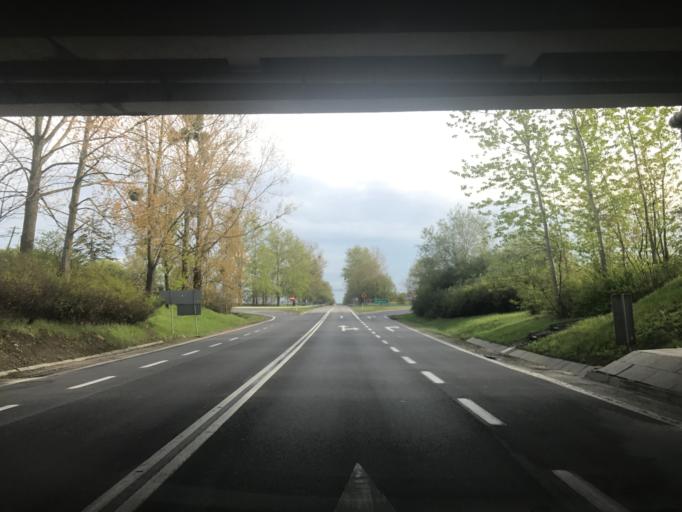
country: PL
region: Pomeranian Voivodeship
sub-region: Powiat tczewski
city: Subkowy
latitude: 54.0484
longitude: 18.7611
